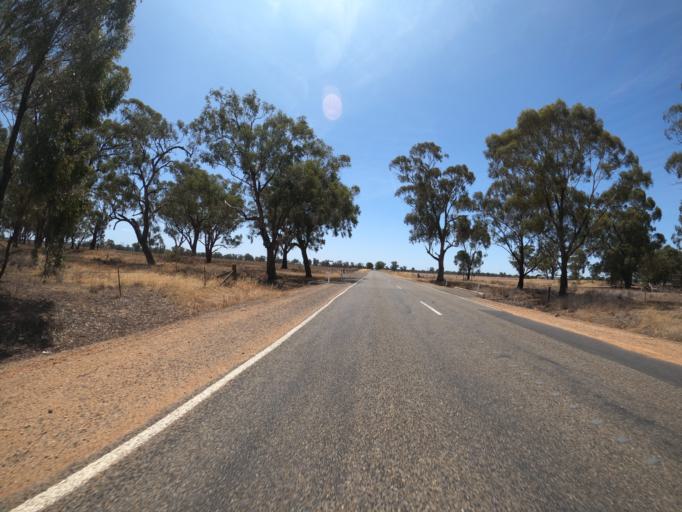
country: AU
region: Victoria
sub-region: Moira
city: Yarrawonga
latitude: -36.1793
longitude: 145.9672
